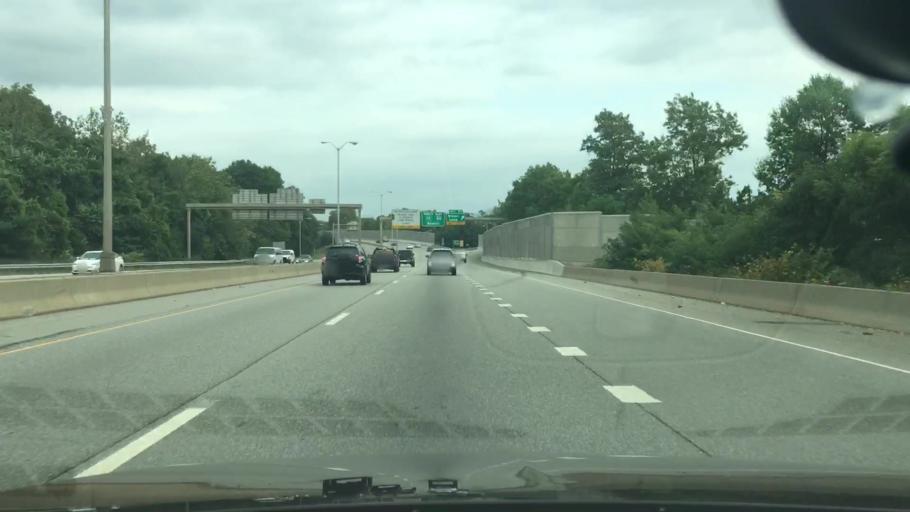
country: US
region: Connecticut
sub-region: Hartford County
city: East Hartford
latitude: 41.7590
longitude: -72.6422
